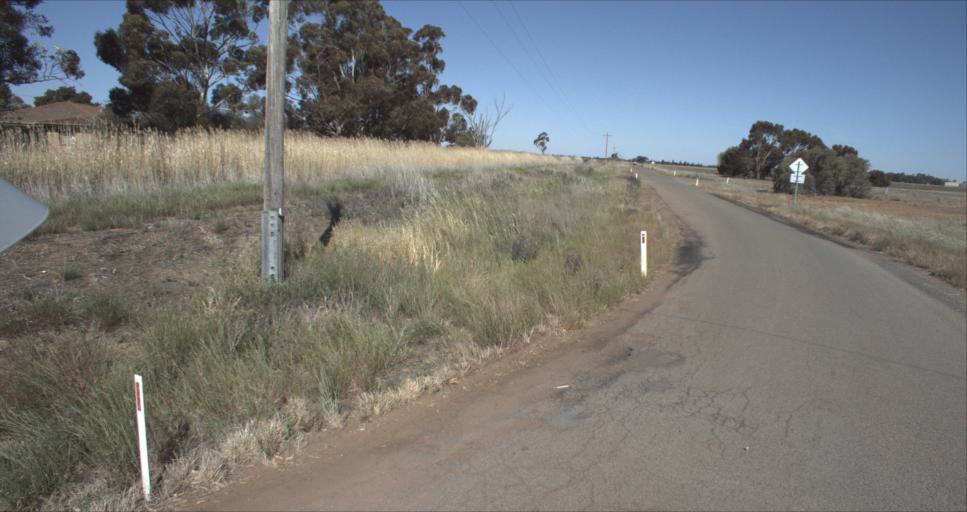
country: AU
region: New South Wales
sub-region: Leeton
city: Leeton
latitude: -34.4781
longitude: 146.3680
